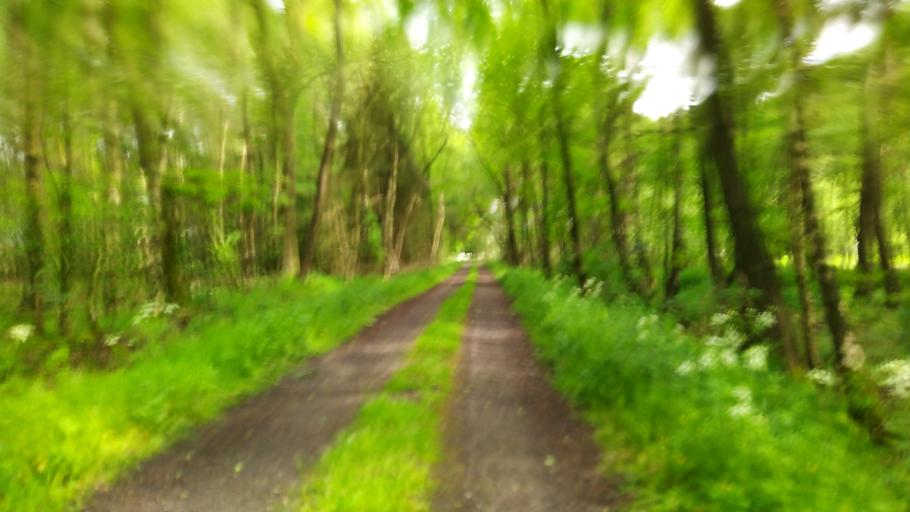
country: DE
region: Lower Saxony
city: Brest
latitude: 53.4233
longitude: 9.3567
